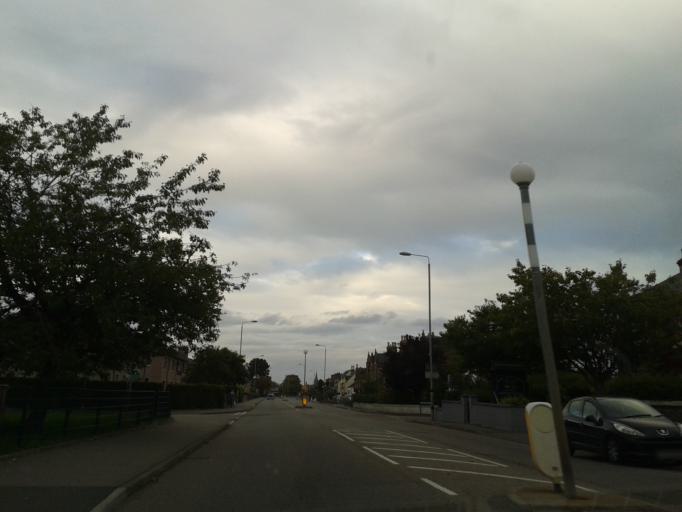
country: GB
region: Scotland
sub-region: Highland
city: Inverness
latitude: 57.4692
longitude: -4.2377
